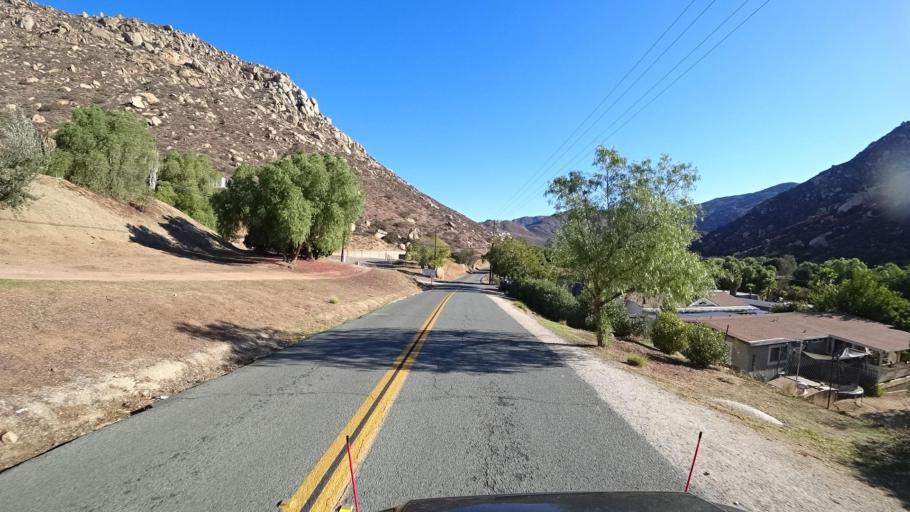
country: MX
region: Baja California
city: Tecate
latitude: 32.6225
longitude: -116.6922
